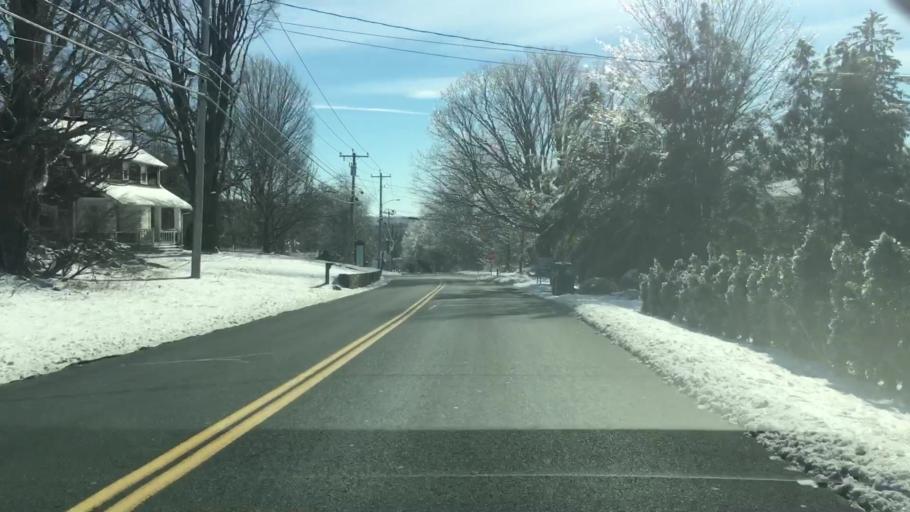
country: US
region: Connecticut
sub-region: Fairfield County
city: Trumbull
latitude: 41.3180
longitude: -73.2198
